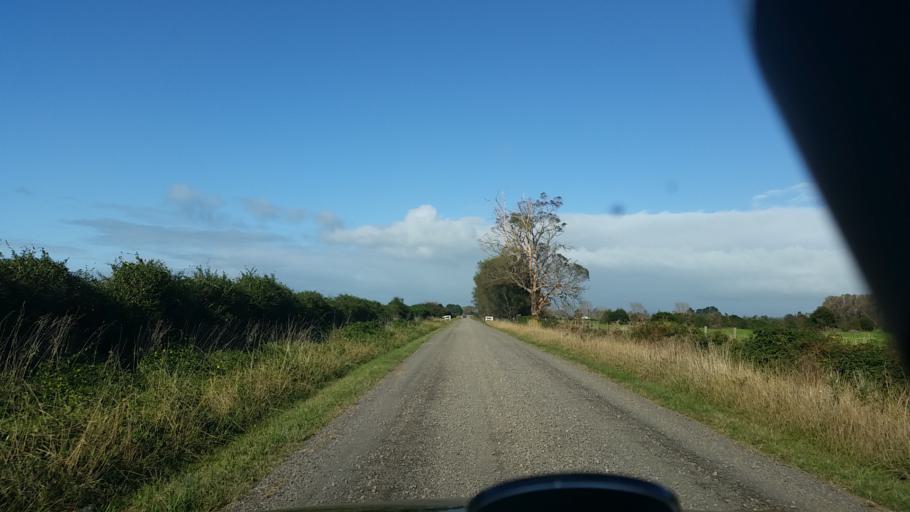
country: NZ
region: Bay of Plenty
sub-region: Western Bay of Plenty District
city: Katikati
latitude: -37.5867
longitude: 175.7131
